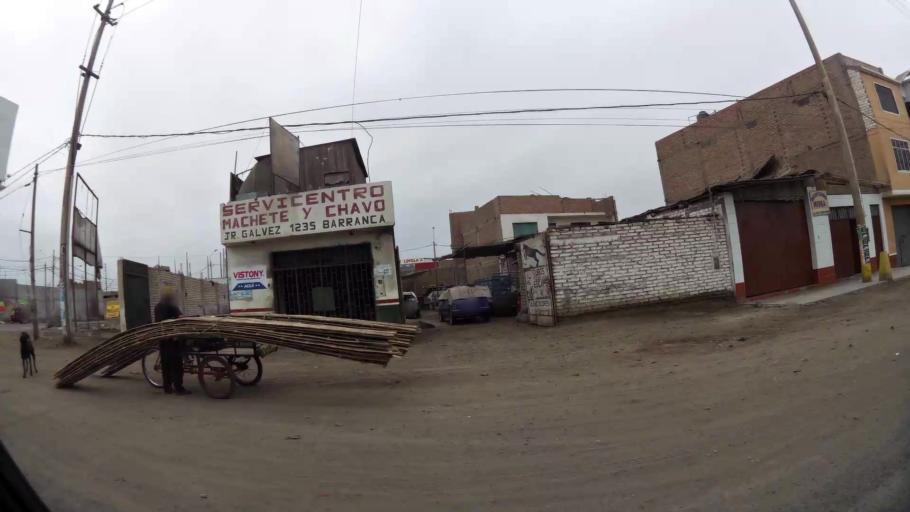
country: PE
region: Lima
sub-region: Barranca
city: Barranca
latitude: -10.7598
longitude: -77.7538
